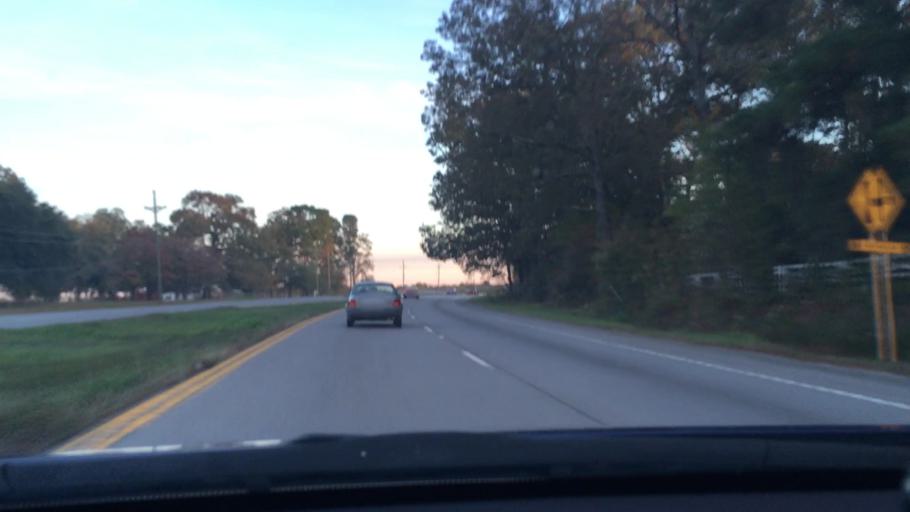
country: US
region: South Carolina
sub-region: Richland County
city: Hopkins
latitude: 33.9463
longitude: -80.8082
